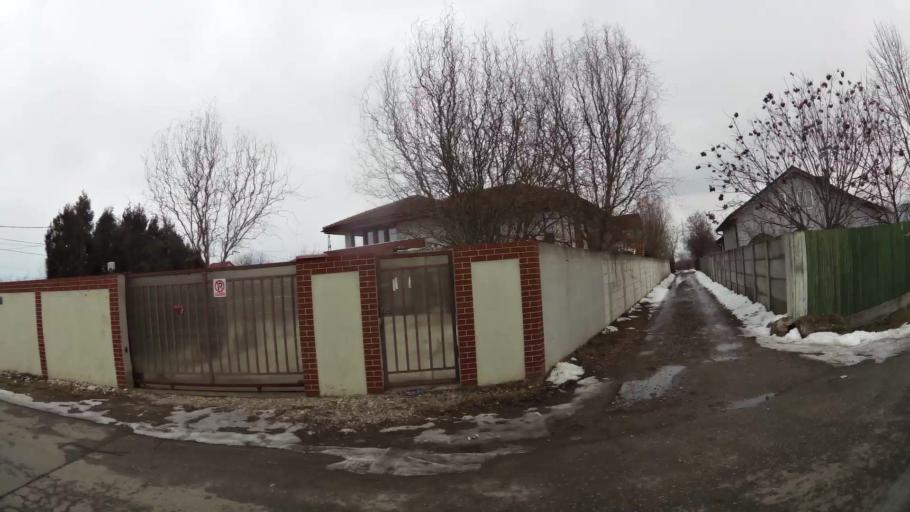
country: RO
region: Ilfov
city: Stefanestii de Jos
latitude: 44.5413
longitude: 26.2105
